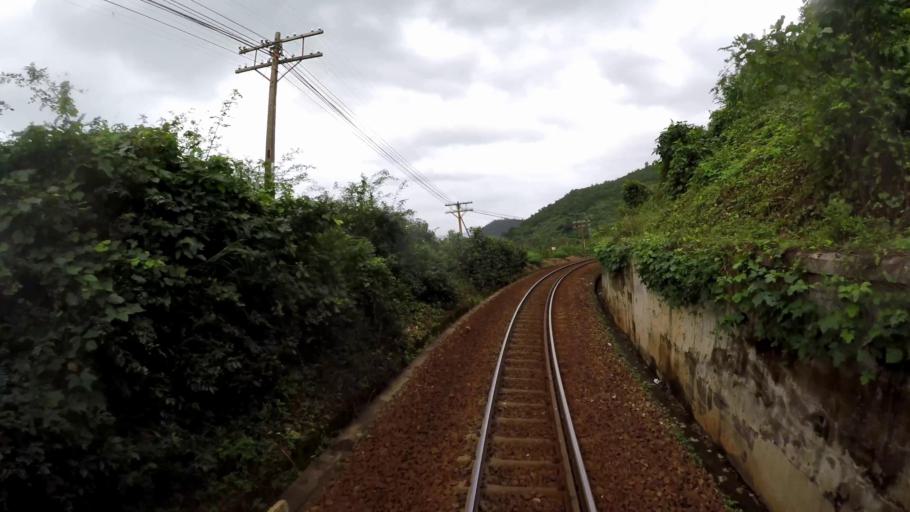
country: VN
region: Da Nang
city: Lien Chieu
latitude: 16.1584
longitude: 108.1351
